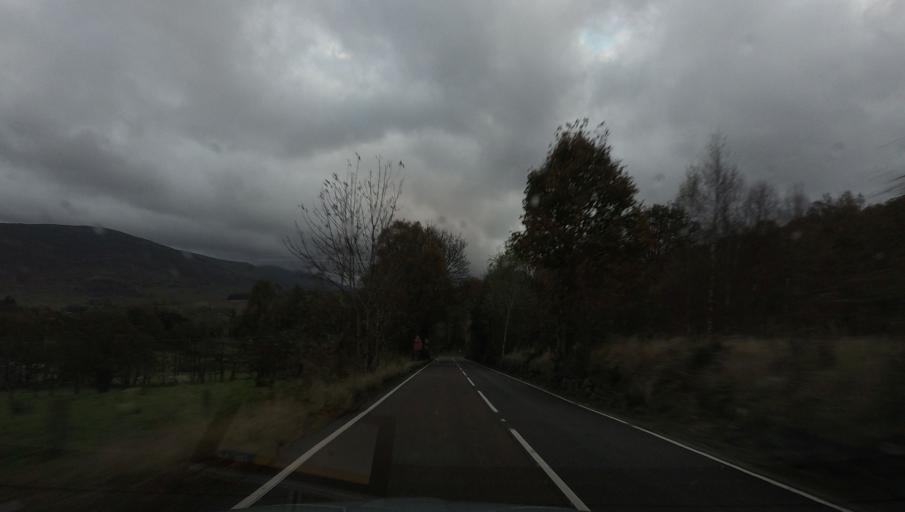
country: GB
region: Scotland
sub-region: Stirling
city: Callander
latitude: 56.3896
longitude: -4.2913
